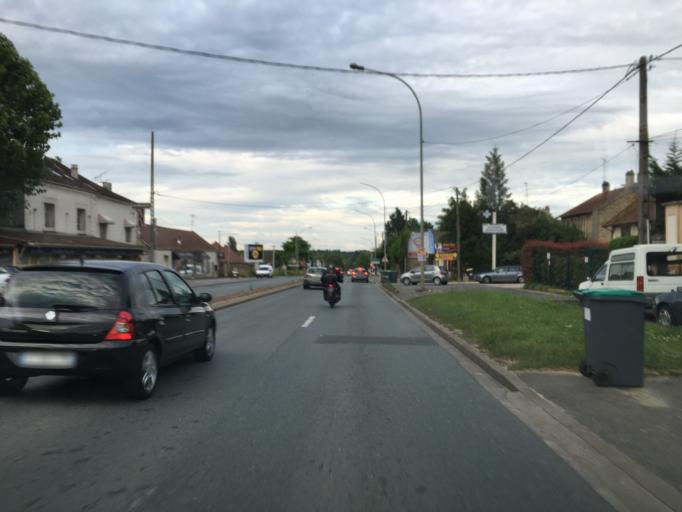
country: FR
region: Ile-de-France
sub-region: Departement du Val-de-Marne
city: Villecresnes
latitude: 48.7273
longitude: 2.5334
